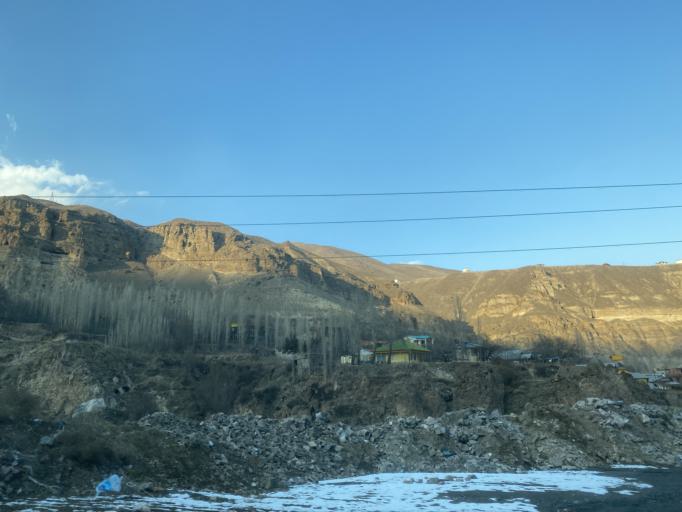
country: IR
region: Tehran
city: Damavand
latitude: 35.8674
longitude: 52.1516
